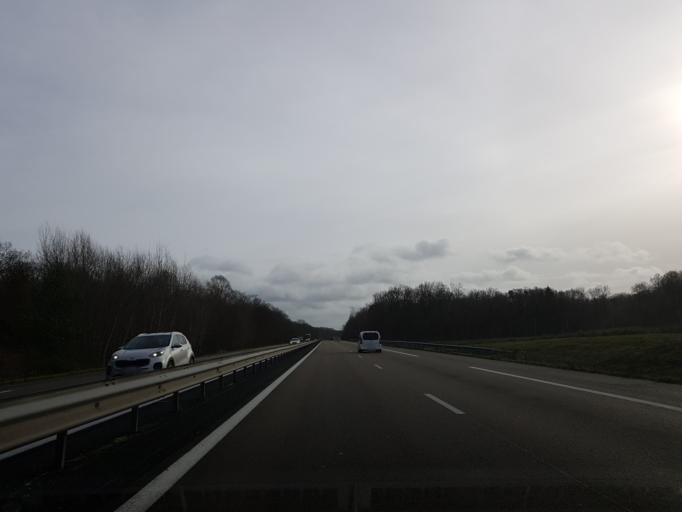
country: FR
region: Champagne-Ardenne
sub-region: Departement de l'Aube
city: Lusigny-sur-Barse
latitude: 48.1984
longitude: 4.2633
